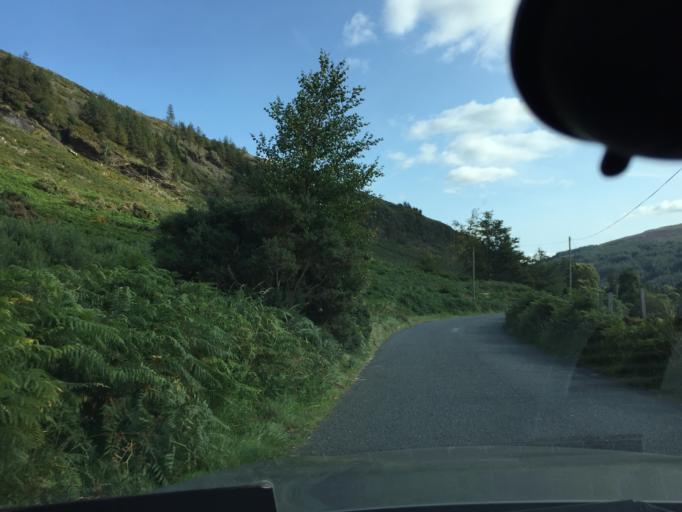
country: IE
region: Leinster
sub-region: Wicklow
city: Rathdrum
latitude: 53.0462
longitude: -6.3278
